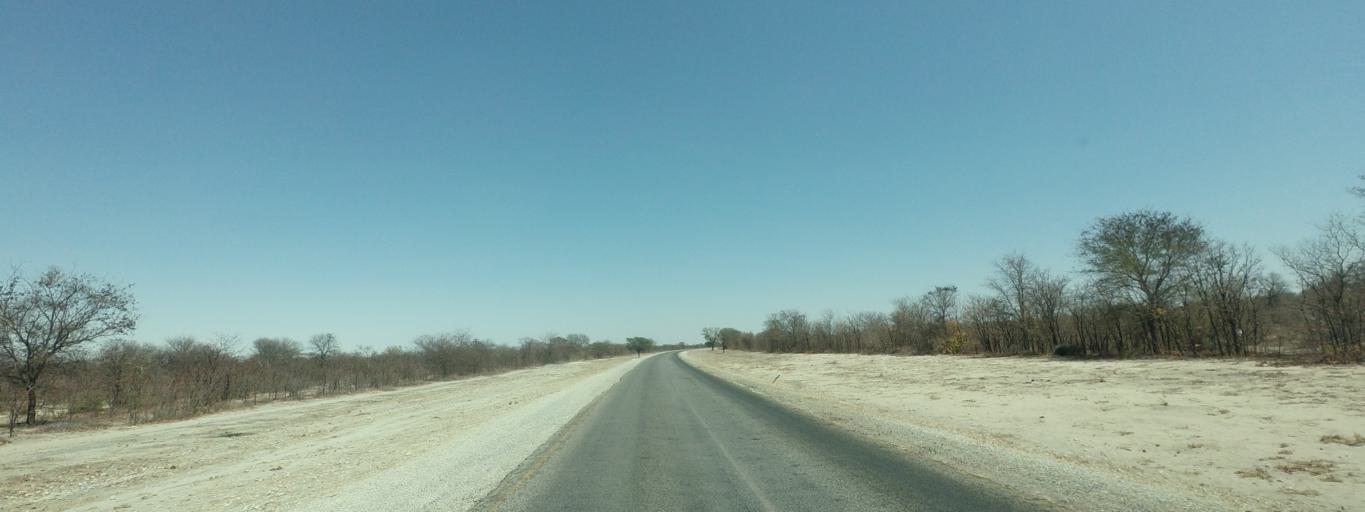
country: BW
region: North East
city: Dukwe
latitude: -20.3848
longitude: 26.3334
